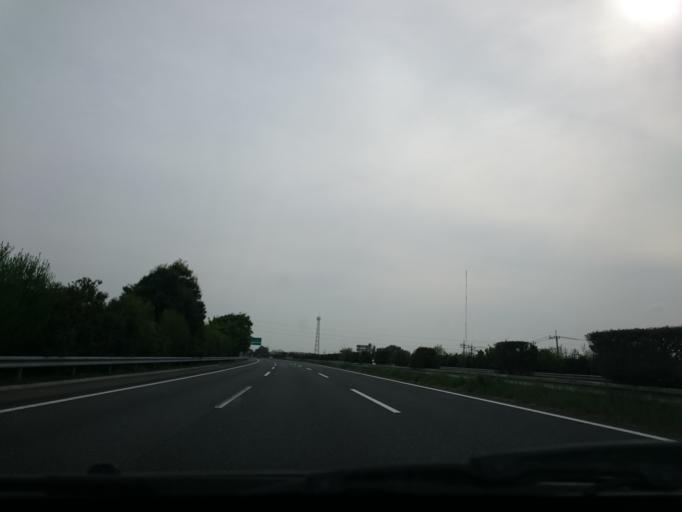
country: JP
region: Tochigi
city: Kanuma
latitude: 36.5507
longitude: 139.8057
